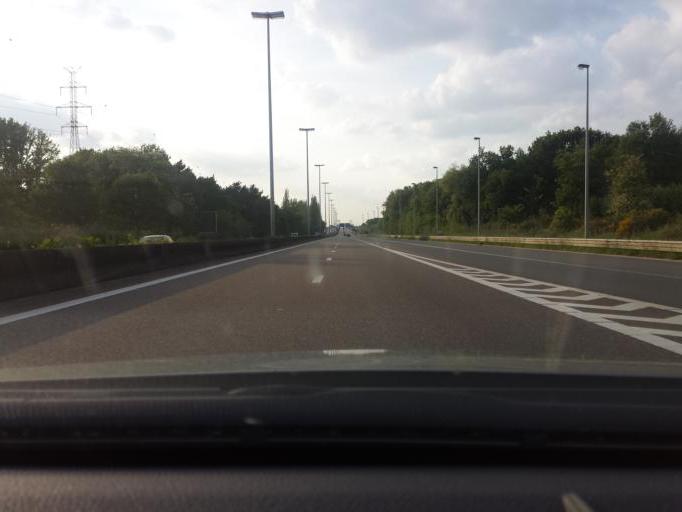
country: BE
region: Flanders
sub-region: Provincie Limburg
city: Lummen
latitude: 50.9836
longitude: 5.2357
